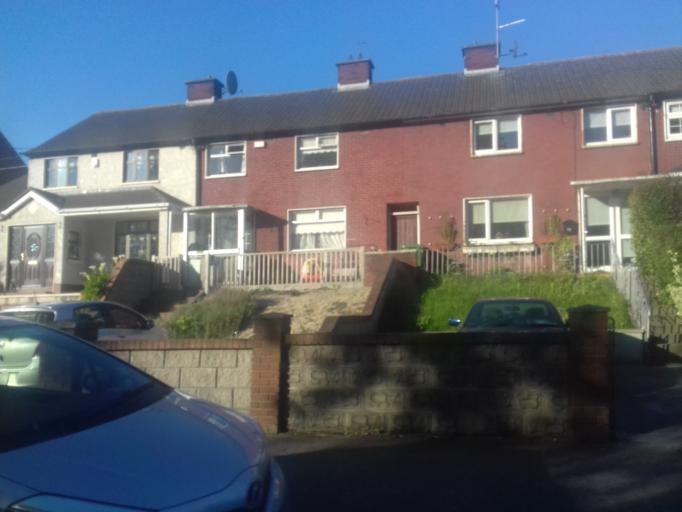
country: IE
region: Leinster
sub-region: Dublin City
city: Finglas
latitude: 53.3861
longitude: -6.2956
